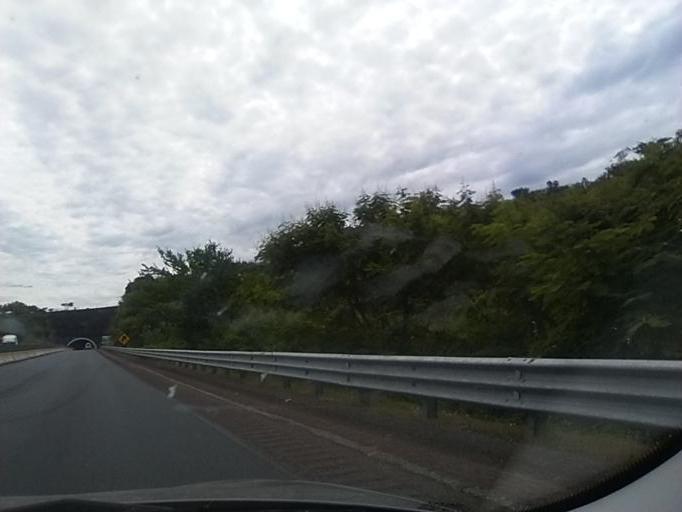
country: MX
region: Guerrero
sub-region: Huitzuco de los Figueroa
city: Ciudad de Huitzuco
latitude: 18.2068
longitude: -99.2102
